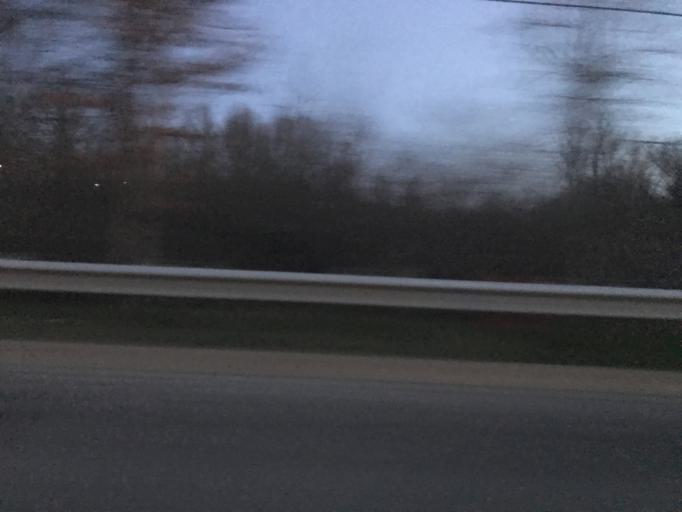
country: US
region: Michigan
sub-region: Livingston County
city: Brighton
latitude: 42.5439
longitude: -83.7939
